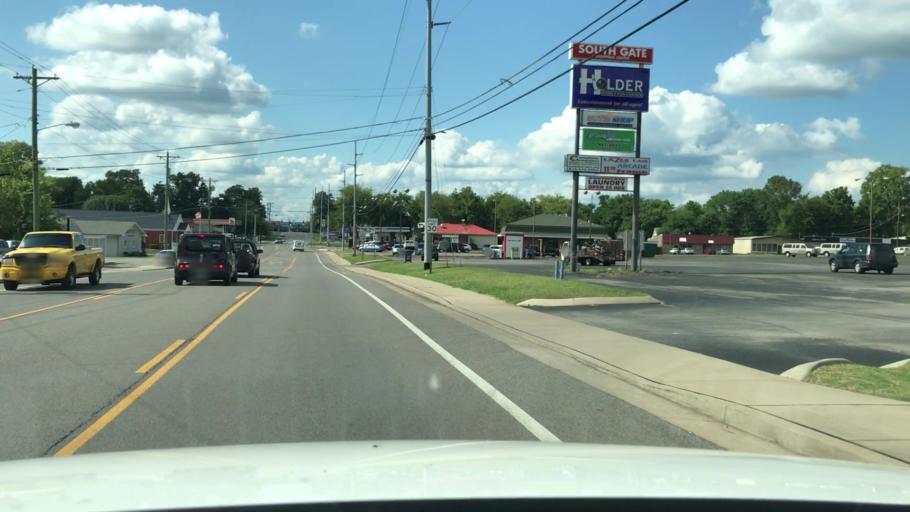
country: US
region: Tennessee
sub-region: Sumner County
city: Gallatin
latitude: 36.3783
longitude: -86.4425
